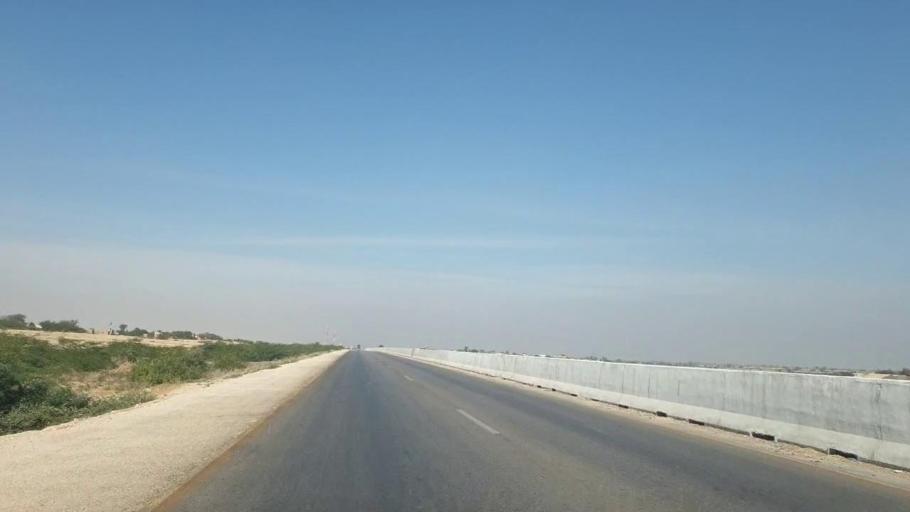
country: PK
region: Sindh
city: Matiari
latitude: 25.6884
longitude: 68.2953
